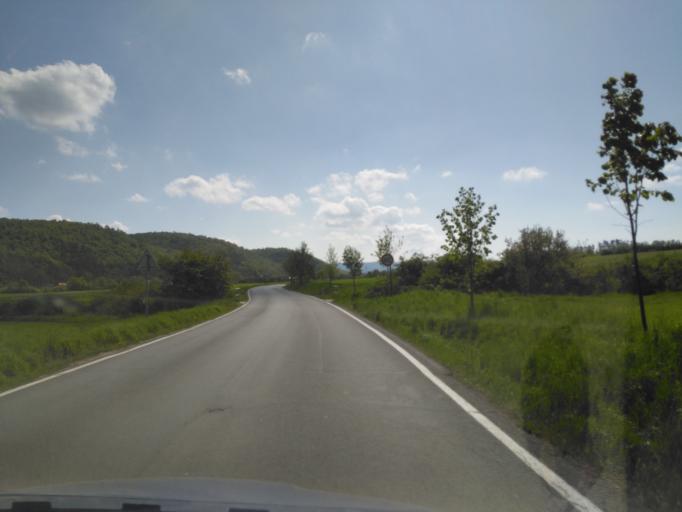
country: CZ
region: Central Bohemia
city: Lochovice
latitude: 49.8796
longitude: 13.9823
